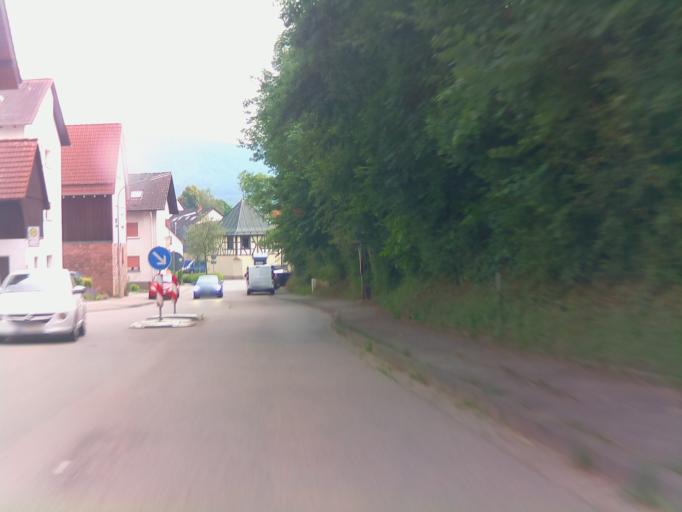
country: DE
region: Hesse
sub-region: Regierungsbezirk Darmstadt
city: Rimbach
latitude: 49.6395
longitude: 8.7570
